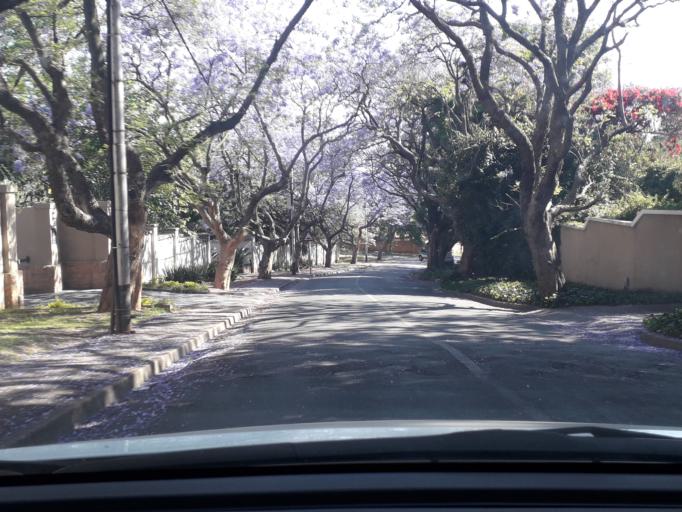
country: ZA
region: Gauteng
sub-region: City of Johannesburg Metropolitan Municipality
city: Johannesburg
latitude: -26.1446
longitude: 27.9783
